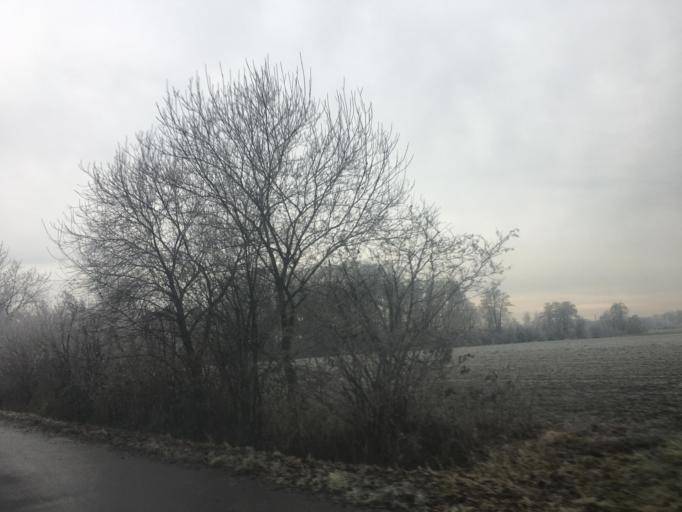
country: DE
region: North Rhine-Westphalia
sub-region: Regierungsbezirk Munster
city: Greven
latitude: 52.0789
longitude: 7.5549
